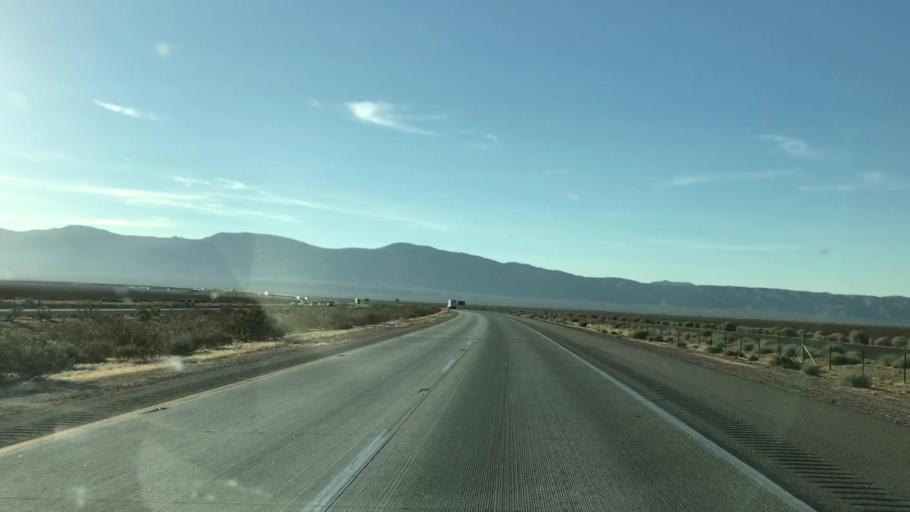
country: US
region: California
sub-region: Kern County
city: Mojave
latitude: 35.0820
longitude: -118.1172
